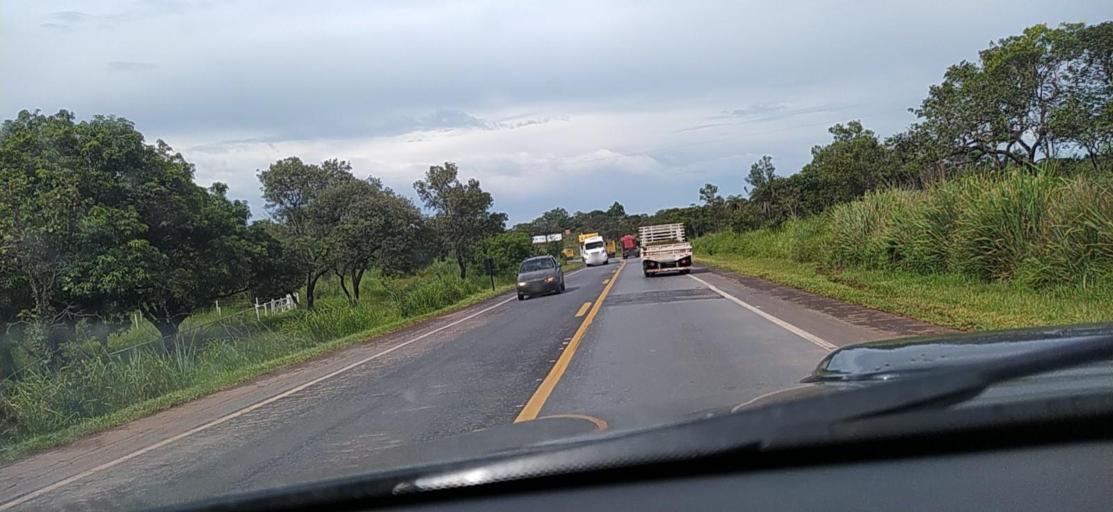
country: BR
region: Minas Gerais
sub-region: Montes Claros
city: Montes Claros
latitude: -16.8727
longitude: -43.8571
